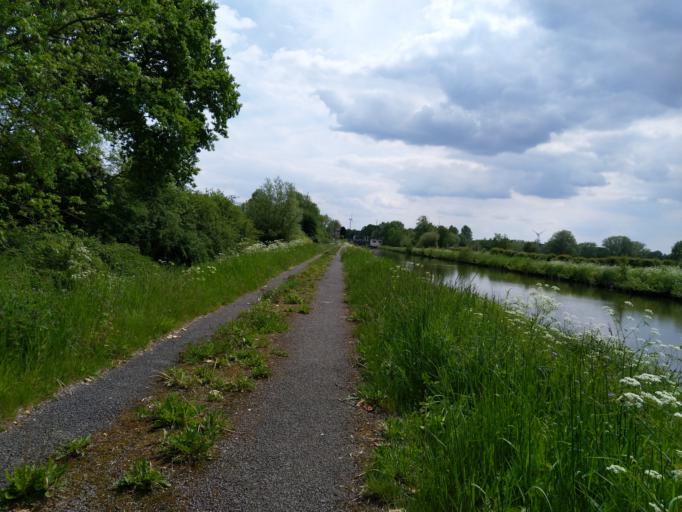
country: FR
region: Picardie
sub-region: Departement de l'Aisne
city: Wassigny
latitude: 50.0506
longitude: 3.6432
